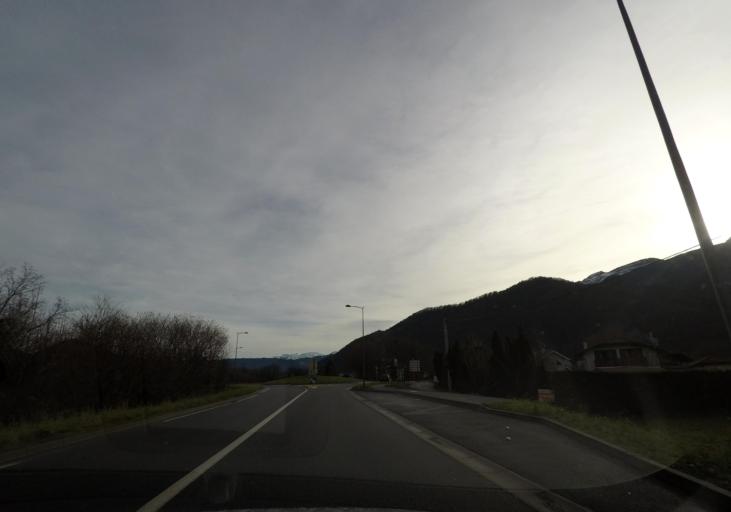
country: FR
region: Rhone-Alpes
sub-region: Departement de la Haute-Savoie
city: Ayse
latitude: 46.0693
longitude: 6.4409
